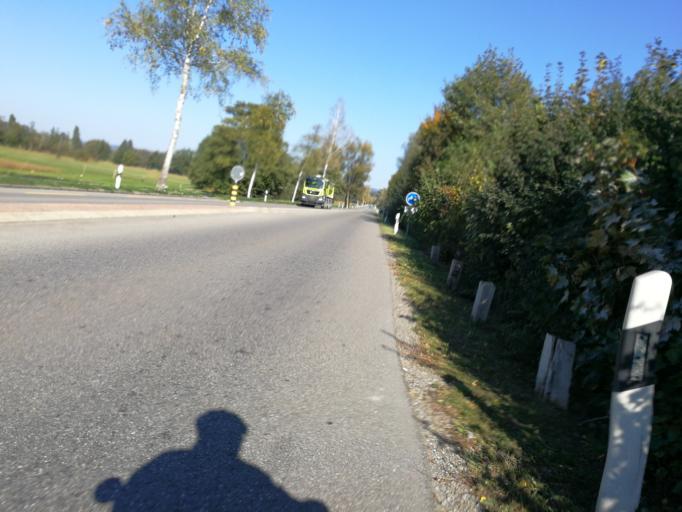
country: CH
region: Zurich
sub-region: Bezirk Uster
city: Hinteregg
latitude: 47.3184
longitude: 8.6999
